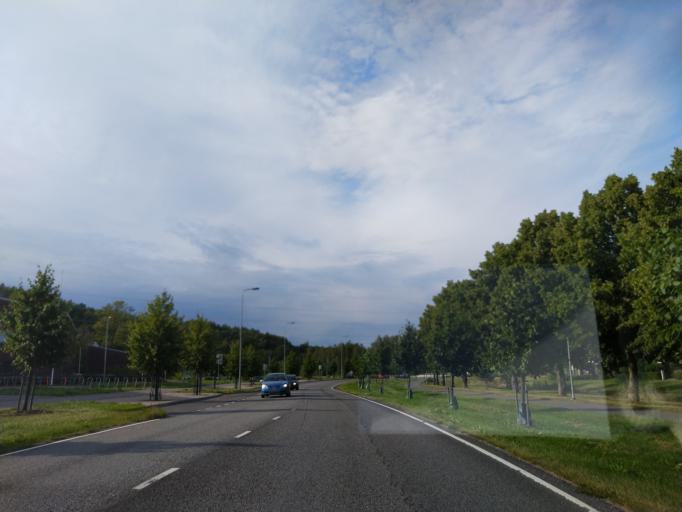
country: FI
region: Varsinais-Suomi
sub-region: Turku
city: Turku
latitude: 60.4197
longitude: 22.2280
